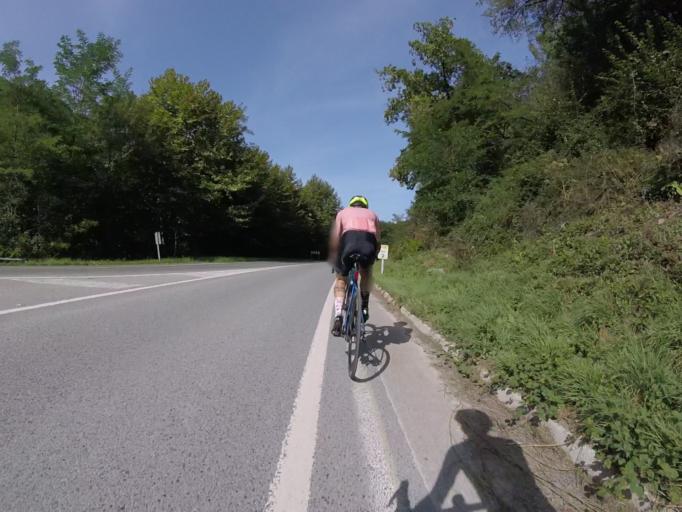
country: ES
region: Navarre
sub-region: Provincia de Navarra
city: Doneztebe
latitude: 43.1409
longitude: -1.5933
